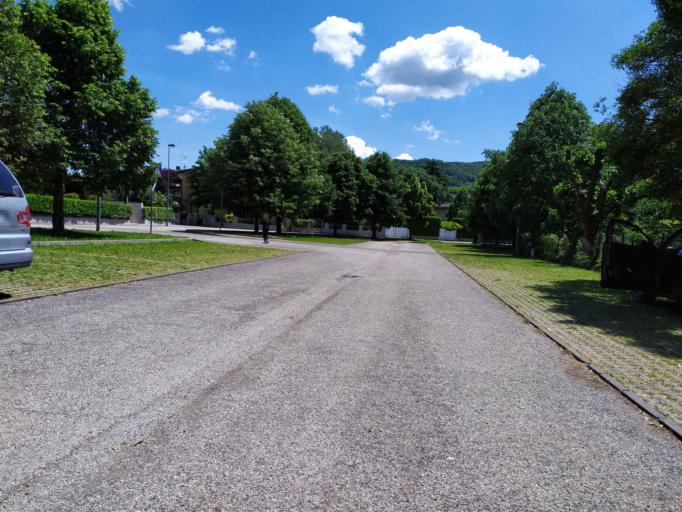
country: IT
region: Veneto
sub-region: Provincia di Vicenza
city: Tavernelle
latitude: 45.5009
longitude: 11.4415
